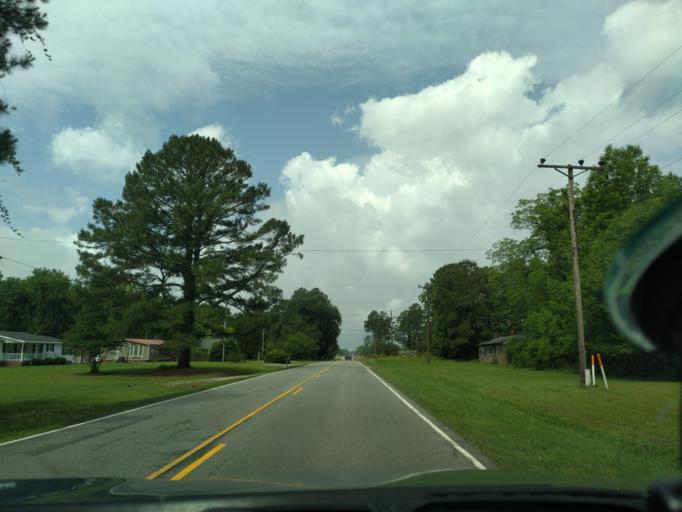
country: US
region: North Carolina
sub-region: Washington County
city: Plymouth
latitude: 35.8744
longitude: -76.6742
